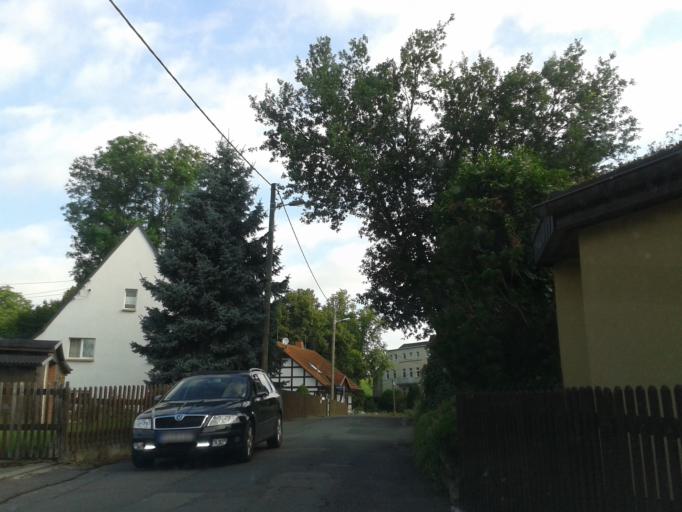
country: DE
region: Saxony
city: Freiberg
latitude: 50.9274
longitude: 13.3421
